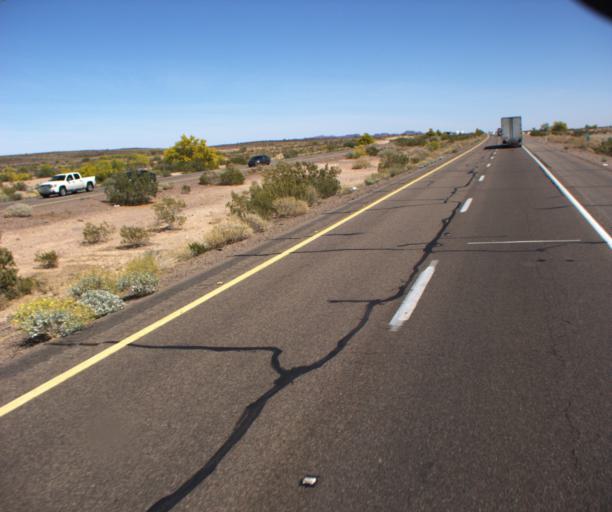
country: US
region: Arizona
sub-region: Maricopa County
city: Gila Bend
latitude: 32.8681
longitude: -113.1471
